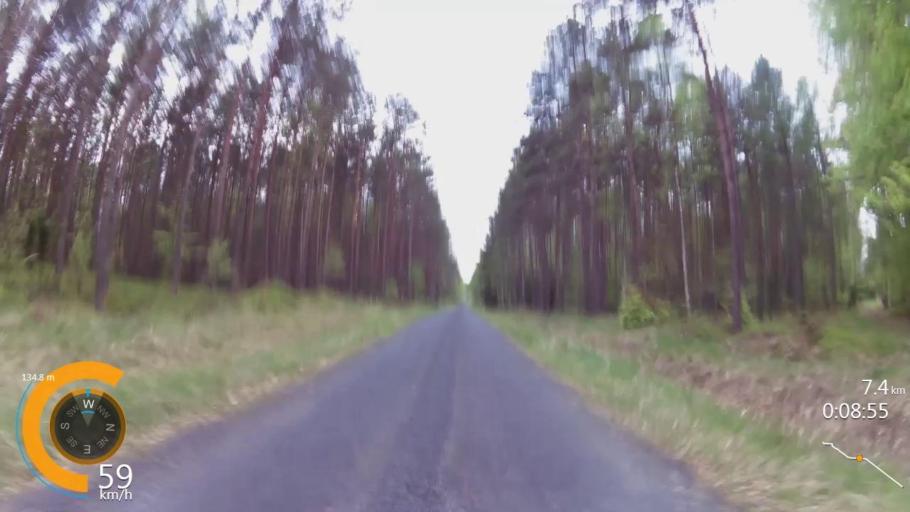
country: PL
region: West Pomeranian Voivodeship
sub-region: Powiat drawski
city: Wierzchowo
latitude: 53.5036
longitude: 16.1438
